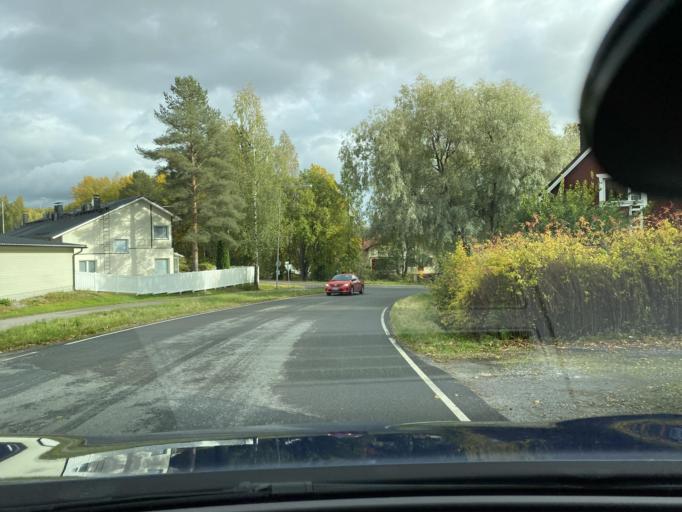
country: FI
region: Pirkanmaa
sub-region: Tampere
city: Nokia
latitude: 61.4765
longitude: 23.3421
